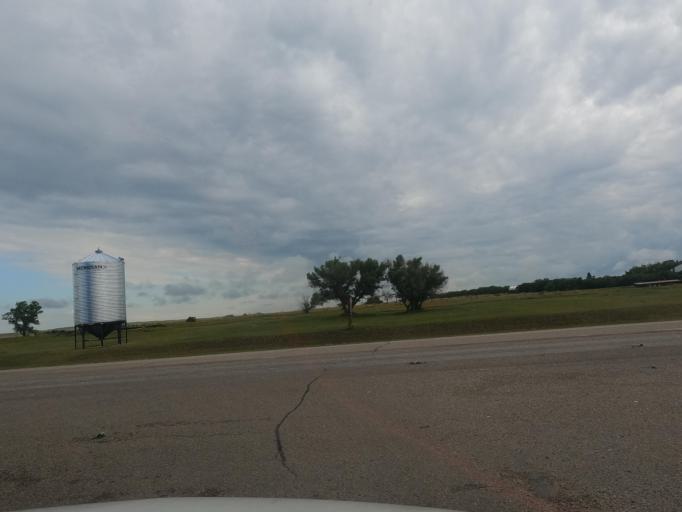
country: CA
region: Saskatchewan
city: Gravelbourg
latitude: 49.6885
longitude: -107.1371
